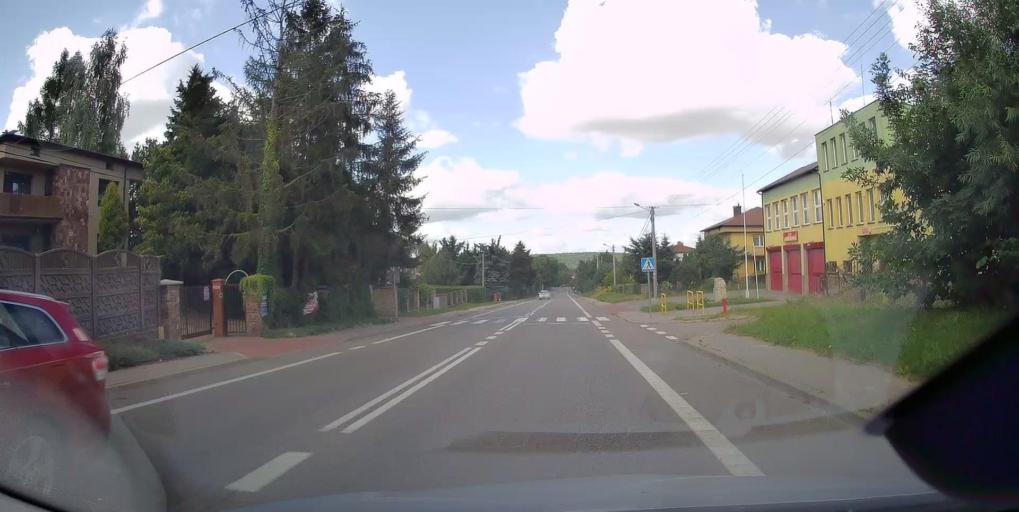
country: PL
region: Swietokrzyskie
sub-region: Powiat kielecki
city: Nowa Slupia
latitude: 50.8589
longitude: 21.0882
